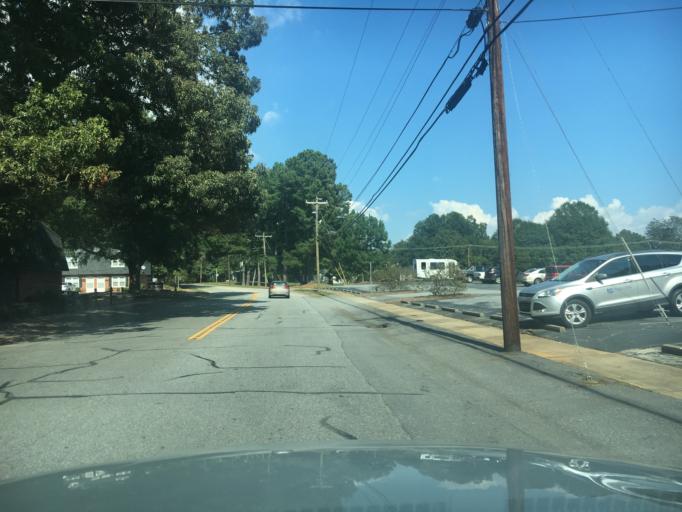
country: US
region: South Carolina
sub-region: Anderson County
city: Pendleton
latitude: 34.6523
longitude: -82.7777
